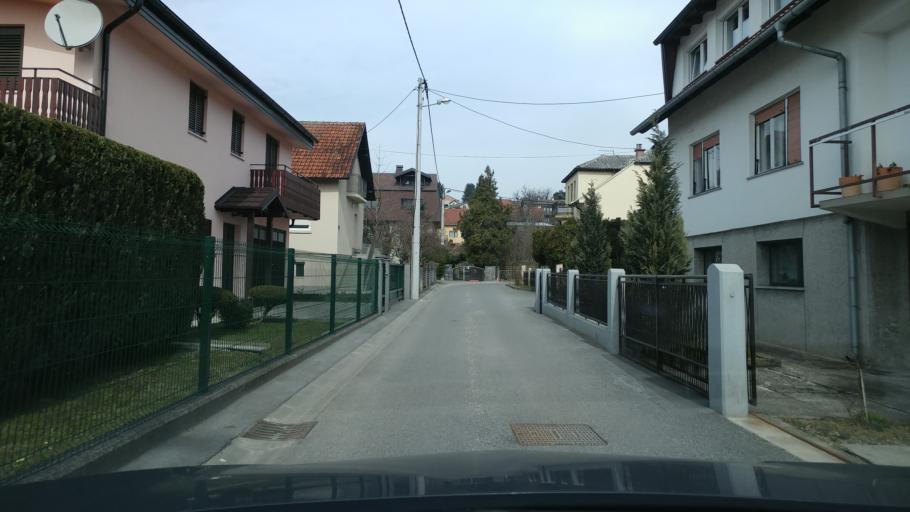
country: HR
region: Grad Zagreb
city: Jezdovec
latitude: 45.8161
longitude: 15.8486
